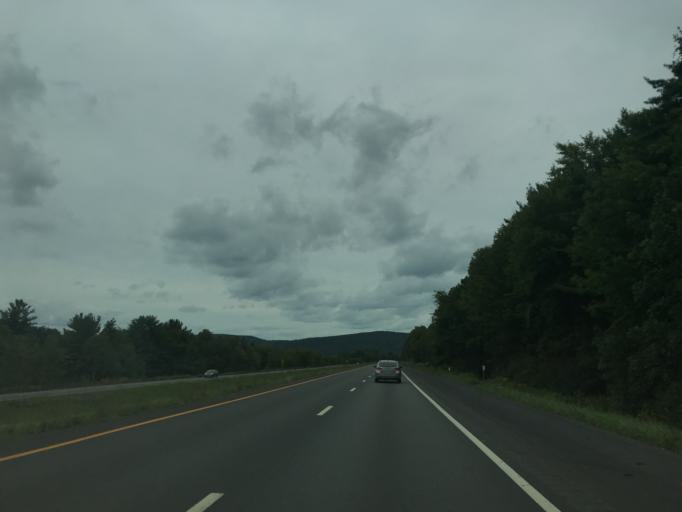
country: US
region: New York
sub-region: Delaware County
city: Sidney
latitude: 42.3000
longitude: -75.3810
